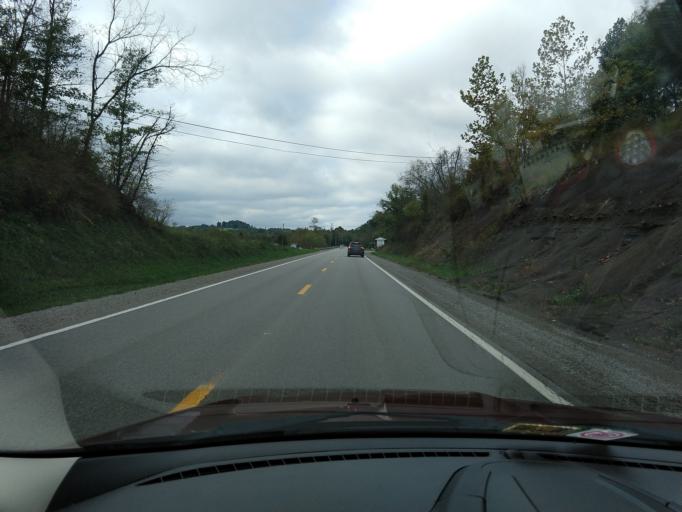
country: US
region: West Virginia
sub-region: Barbour County
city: Belington
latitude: 39.0328
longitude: -79.9449
